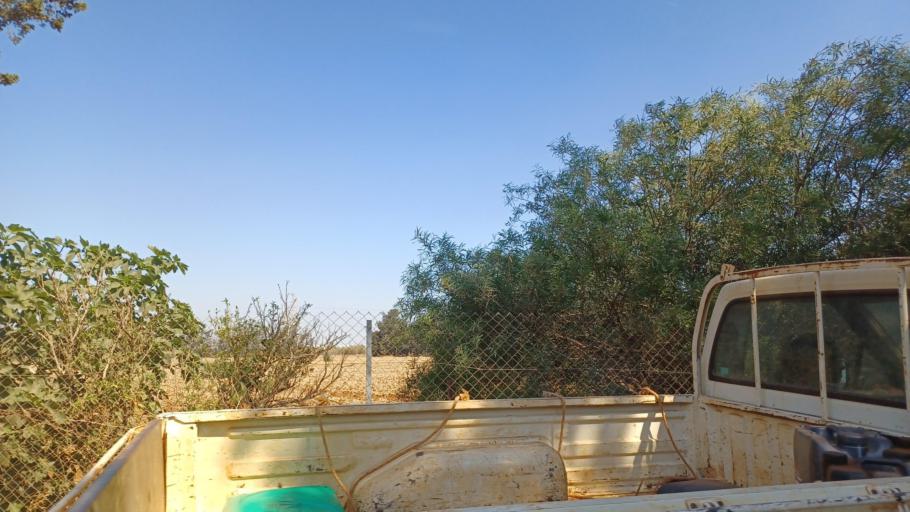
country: CY
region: Ammochostos
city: Avgorou
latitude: 35.0082
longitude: 33.8142
